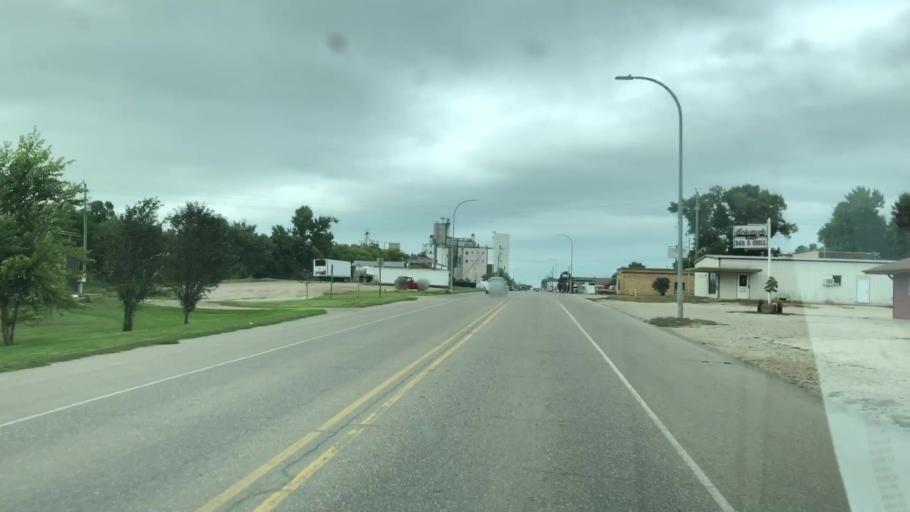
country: US
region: Iowa
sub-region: O'Brien County
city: Sheldon
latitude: 43.1742
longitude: -95.8591
